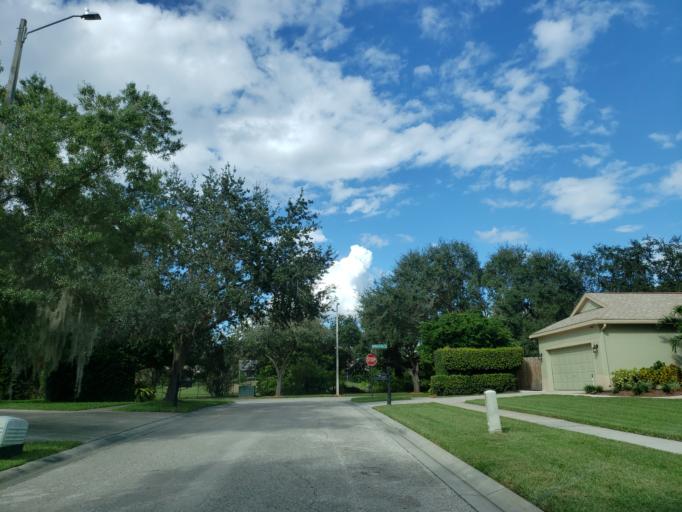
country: US
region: Florida
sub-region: Hillsborough County
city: Bloomingdale
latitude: 27.8738
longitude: -82.2480
